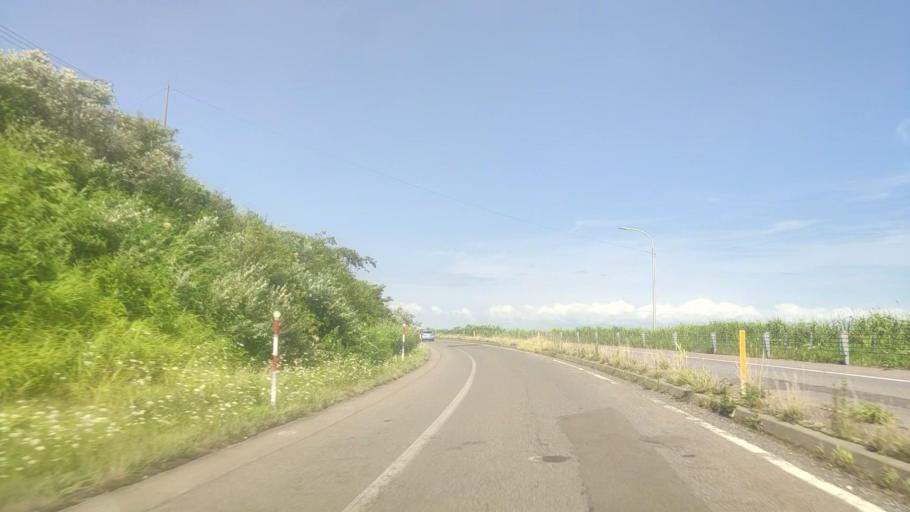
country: JP
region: Hokkaido
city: Nanae
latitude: 42.1978
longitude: 140.4189
